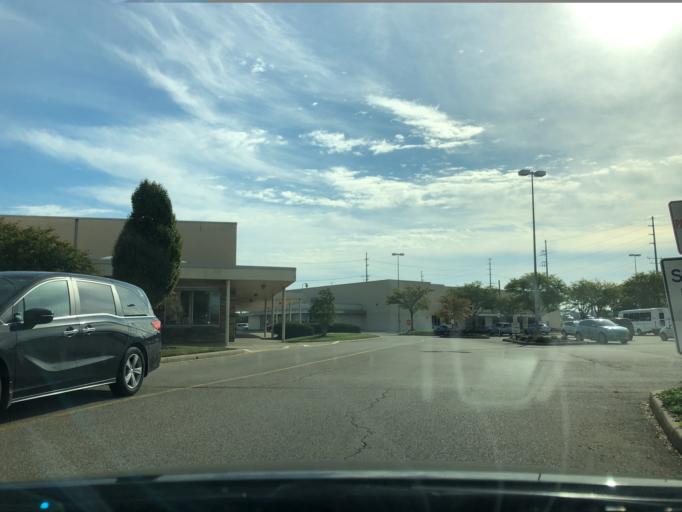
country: US
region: Ohio
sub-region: Hamilton County
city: Glendale
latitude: 39.2885
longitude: -84.4625
